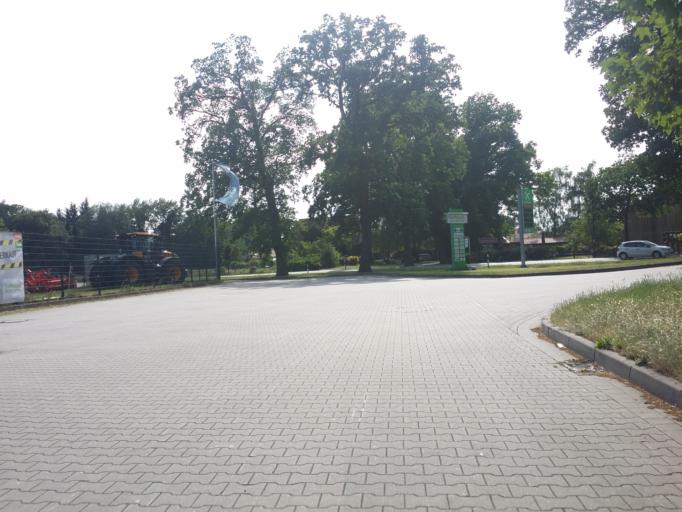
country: DE
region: Lower Saxony
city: Wiefelstede
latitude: 53.3011
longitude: 8.0616
